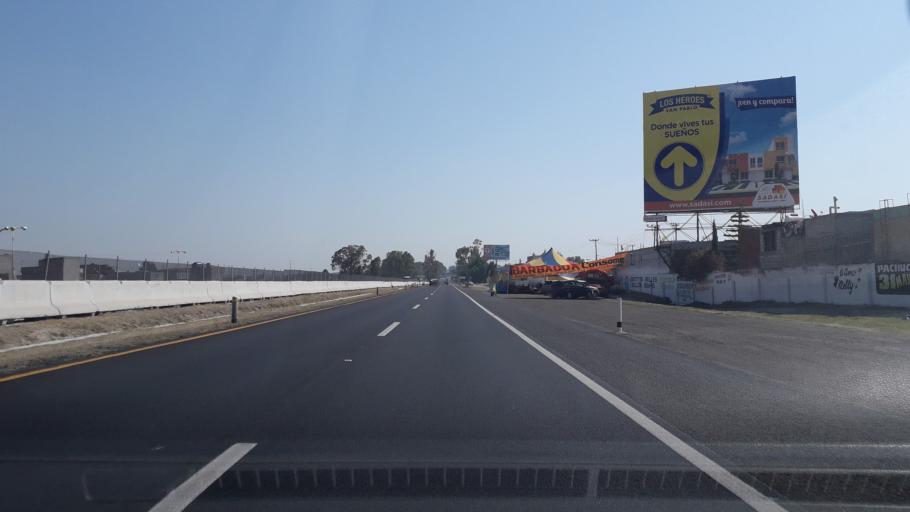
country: MX
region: Mexico
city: Santo Tomas Chiconautla
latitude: 19.6371
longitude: -99.0197
